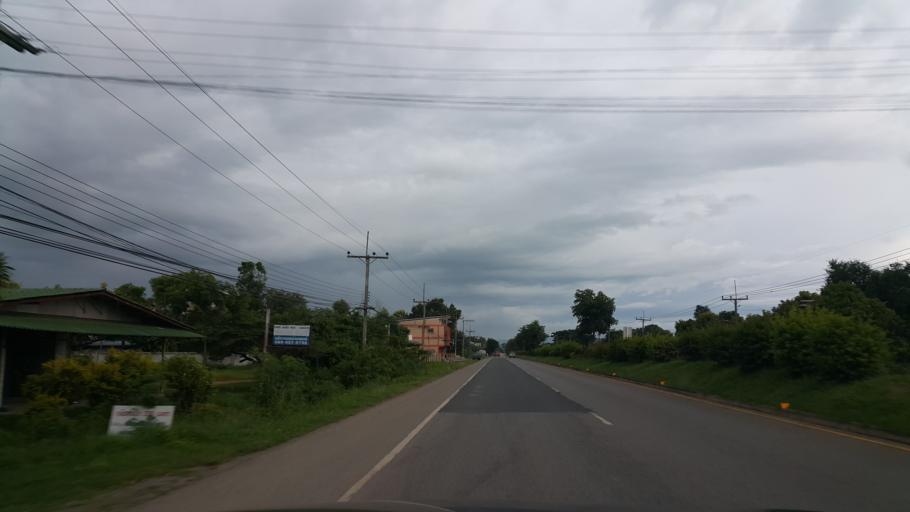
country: TH
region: Phayao
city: Dok Kham Tai
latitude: 19.1469
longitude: 99.9293
